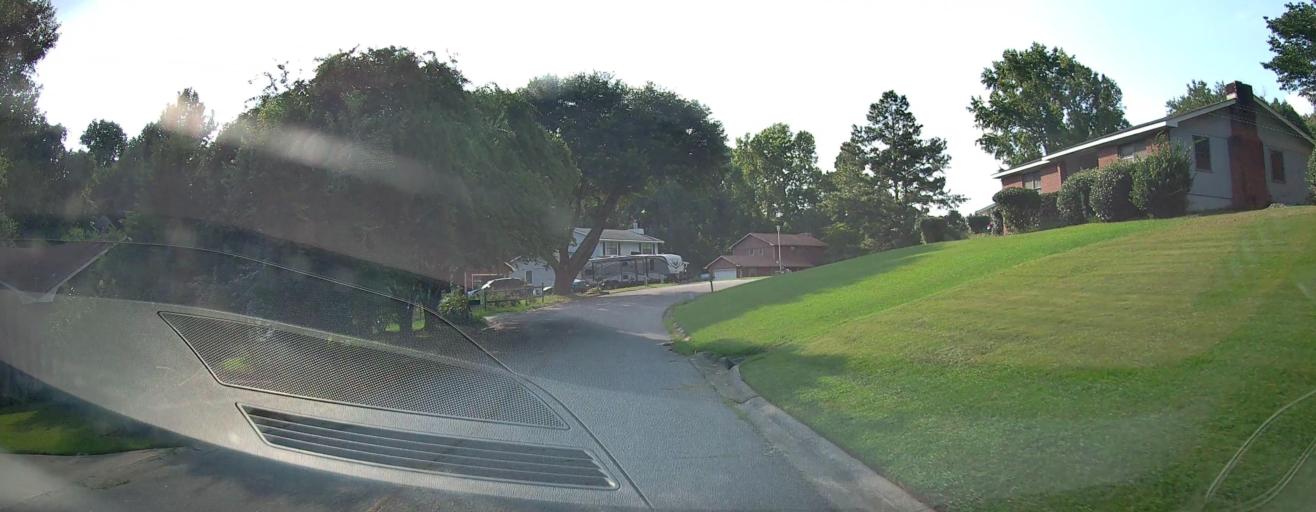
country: US
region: Georgia
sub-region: Houston County
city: Warner Robins
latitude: 32.5835
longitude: -83.6466
